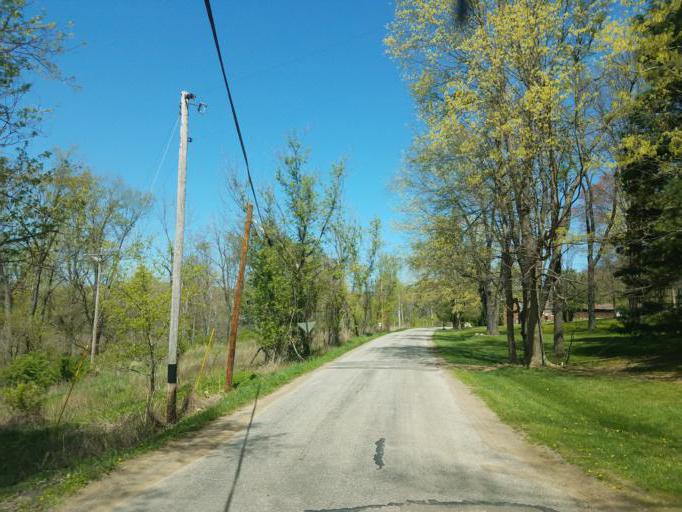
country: US
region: Ohio
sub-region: Richland County
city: Lincoln Heights
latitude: 40.7277
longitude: -82.3999
